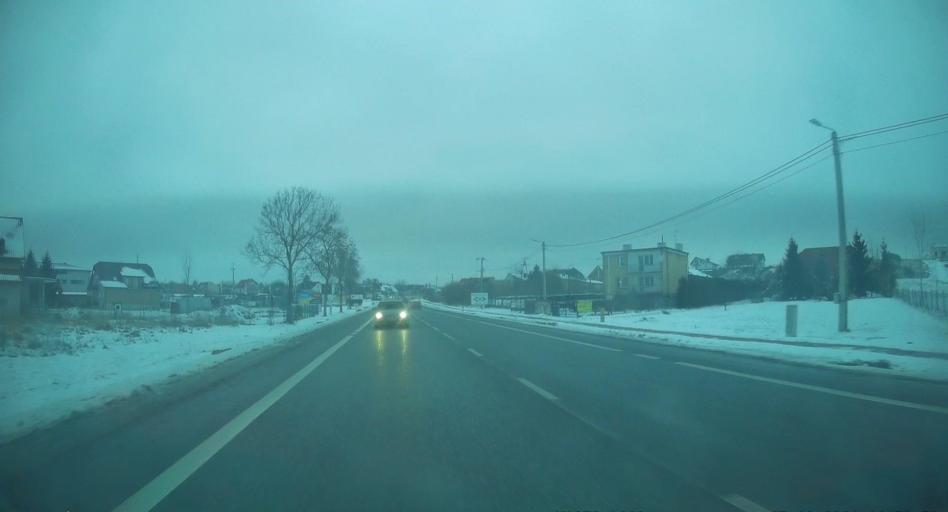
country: PL
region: Swietokrzyskie
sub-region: Powiat kielecki
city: Kostomloty Drugie
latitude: 50.9232
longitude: 20.5674
